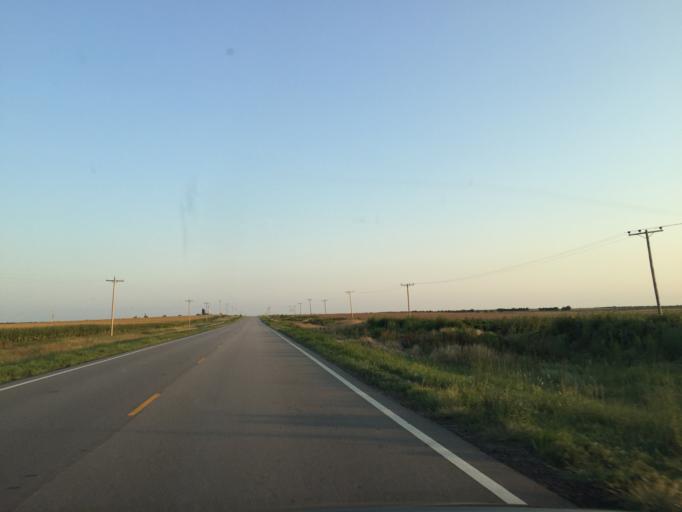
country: US
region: Kansas
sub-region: Ellsworth County
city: Ellsworth
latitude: 38.5572
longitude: -98.2017
